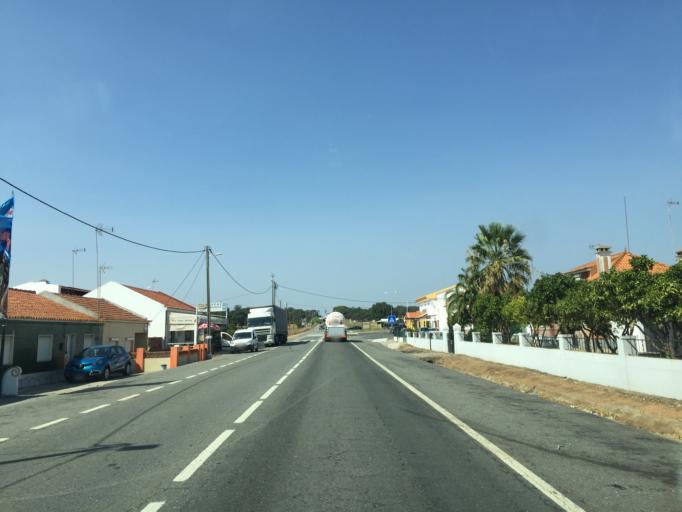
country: PT
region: Beja
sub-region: Aljustrel
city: Aljustrel
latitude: 37.9477
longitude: -8.3807
